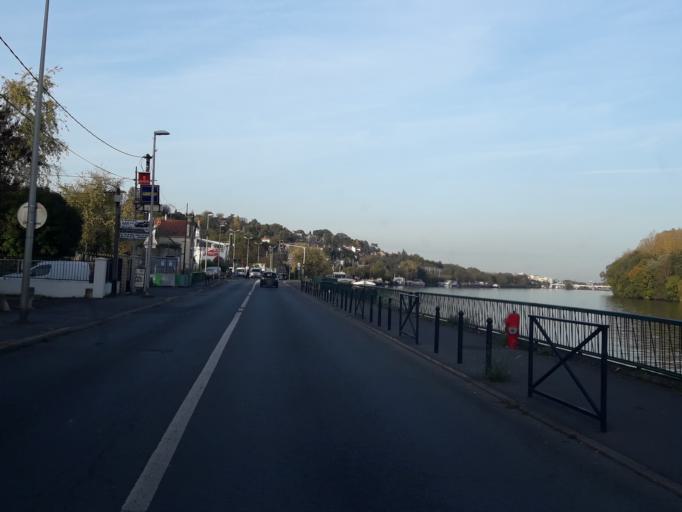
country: FR
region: Ile-de-France
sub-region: Departement de l'Essonne
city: Vigneux-sur-Seine
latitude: 48.7108
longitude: 2.4034
